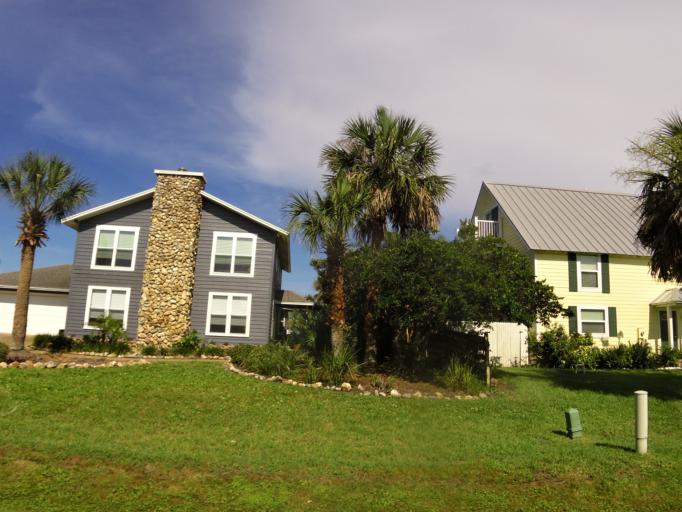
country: US
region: Florida
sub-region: Saint Johns County
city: Villano Beach
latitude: 29.9135
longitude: -81.2967
